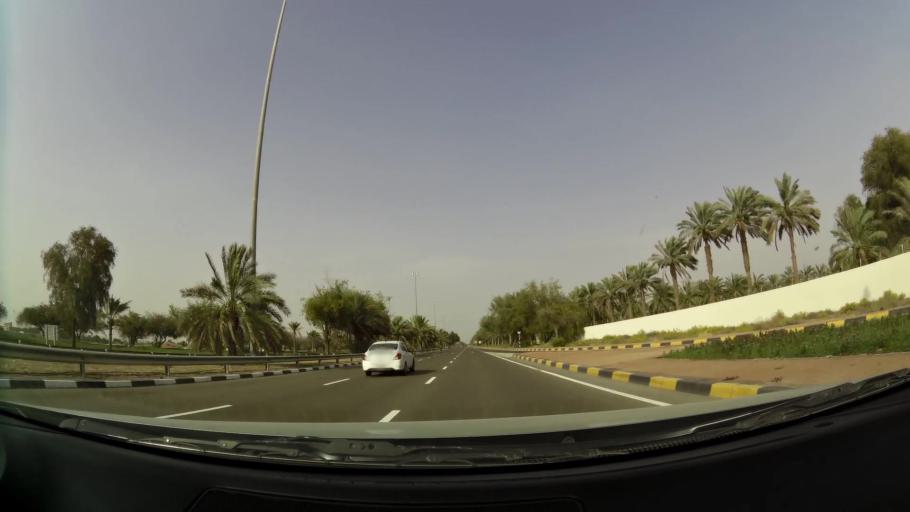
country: AE
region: Abu Dhabi
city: Al Ain
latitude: 24.1864
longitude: 55.6018
